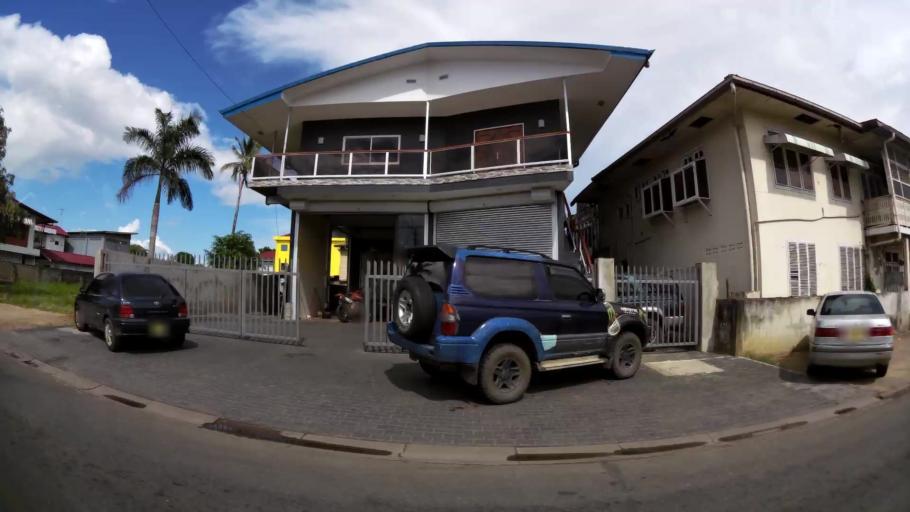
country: SR
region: Paramaribo
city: Paramaribo
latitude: 5.8365
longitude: -55.1505
